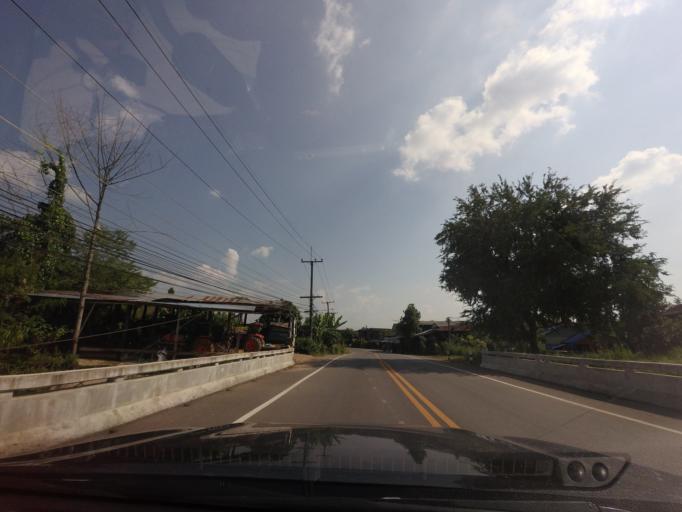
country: TH
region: Nan
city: Santi Suk
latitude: 18.9403
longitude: 100.9244
